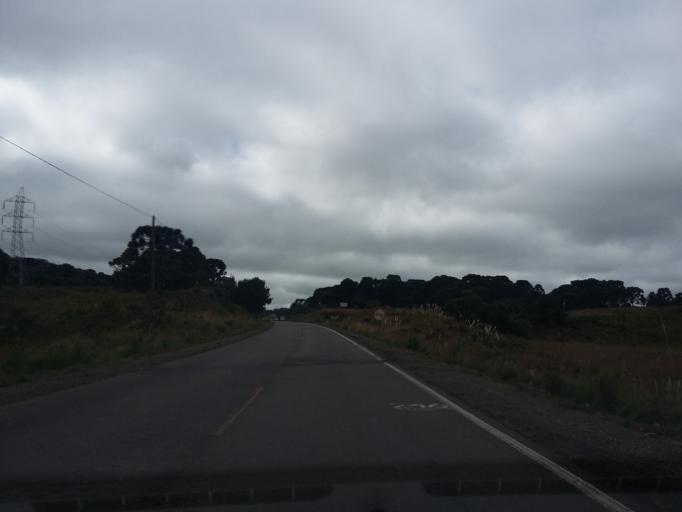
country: BR
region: Santa Catarina
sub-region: Lages
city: Lages
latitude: -27.8819
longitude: -50.1722
